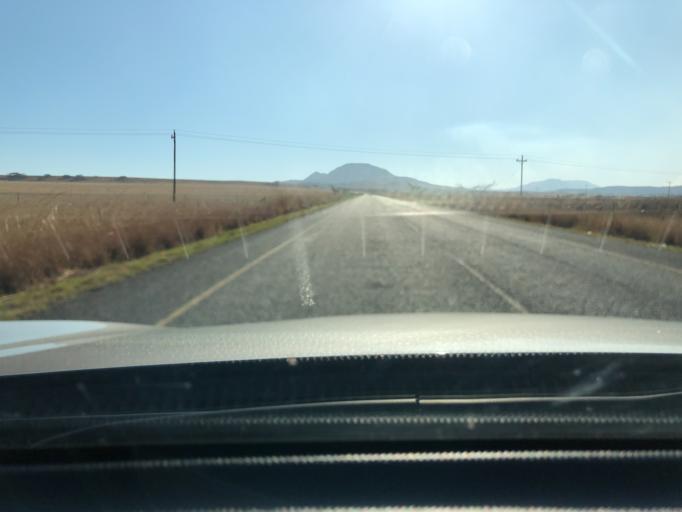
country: ZA
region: KwaZulu-Natal
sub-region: uThukela District Municipality
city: Ekuvukeni
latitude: -28.4060
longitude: 29.9504
